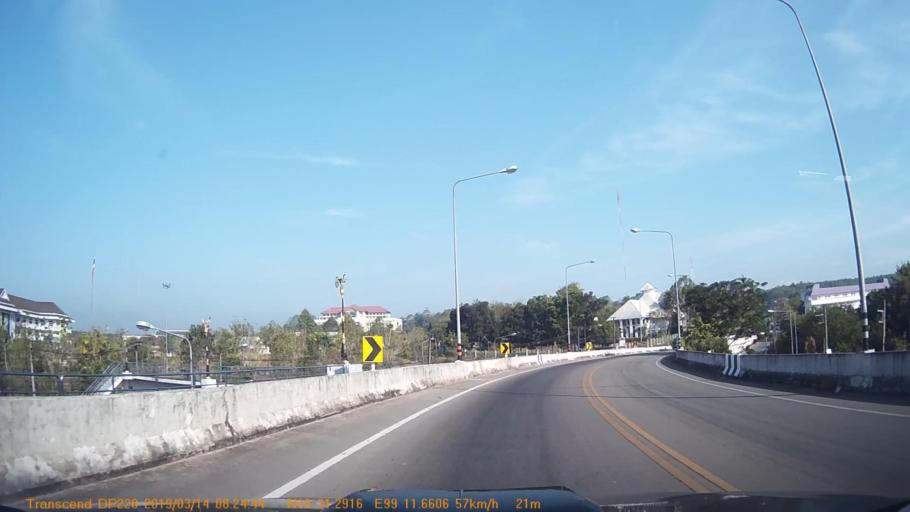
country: TH
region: Chumphon
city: Chumphon
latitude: 10.5217
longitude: 99.1942
